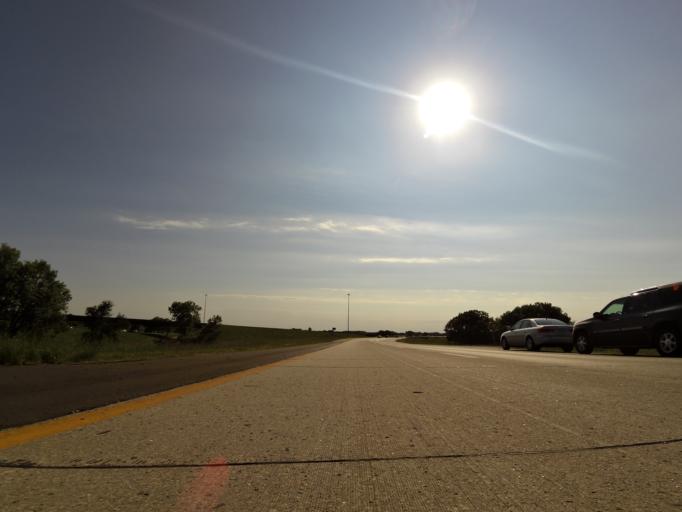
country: US
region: Kansas
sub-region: Sedgwick County
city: Park City
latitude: 37.7567
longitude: -97.3744
